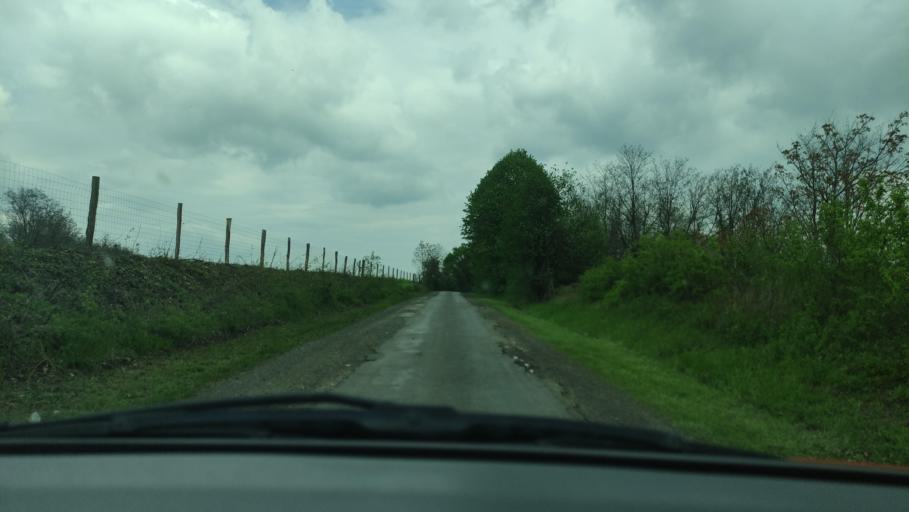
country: HU
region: Somogy
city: Taszar
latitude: 46.2961
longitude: 17.9656
